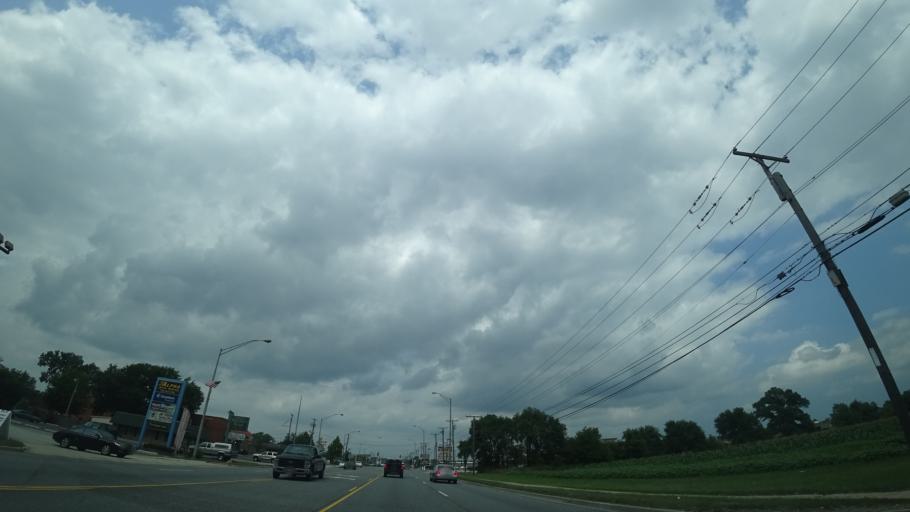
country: US
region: Illinois
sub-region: Cook County
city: Crestwood
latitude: 41.6450
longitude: -87.7380
